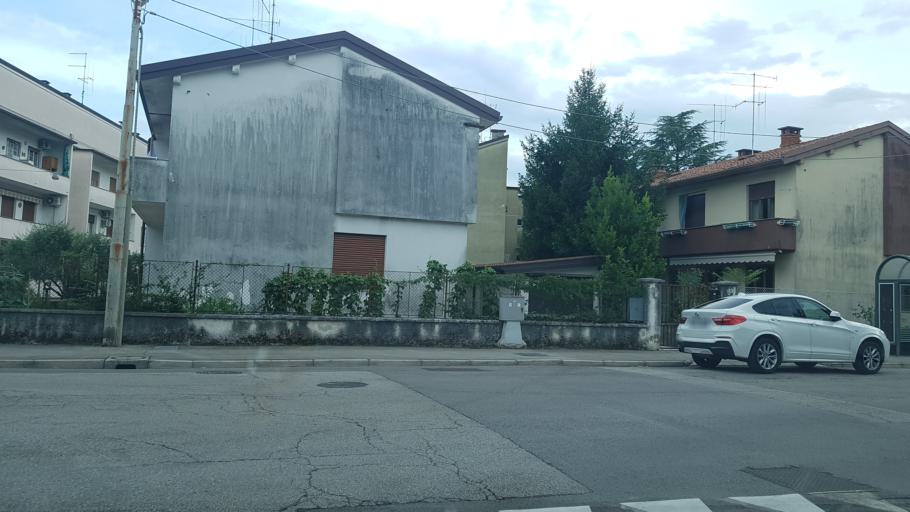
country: IT
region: Friuli Venezia Giulia
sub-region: Provincia di Gorizia
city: Gorizia
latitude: 45.9504
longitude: 13.6119
